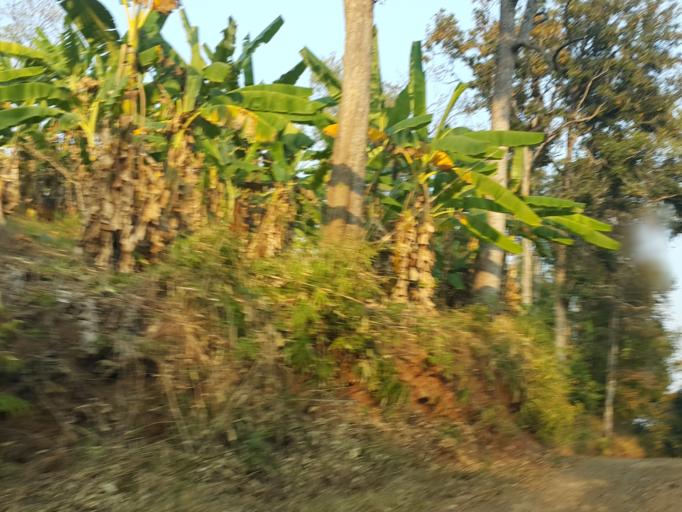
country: TH
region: Chiang Mai
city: Mae Taeng
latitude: 19.0567
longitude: 98.7671
